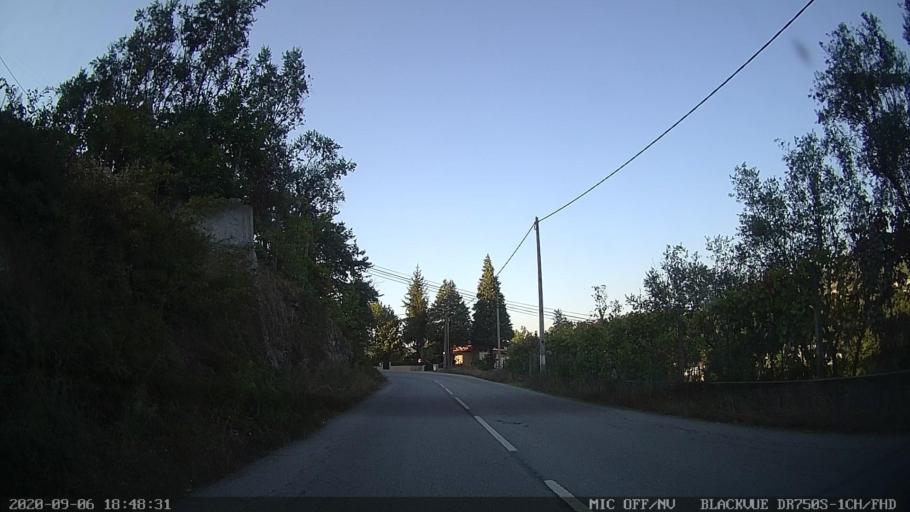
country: PT
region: Porto
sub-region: Amarante
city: Amarante
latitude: 41.2635
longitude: -8.0045
